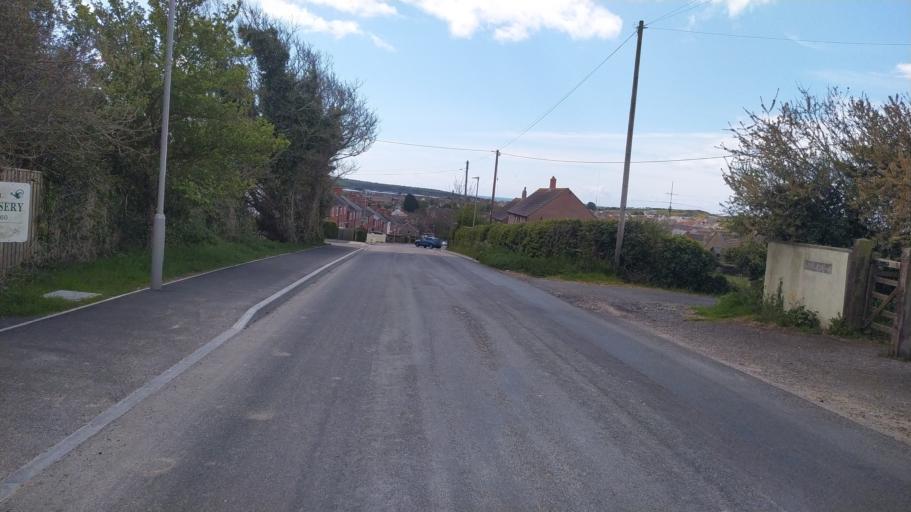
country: GB
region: England
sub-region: Dorset
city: Chickerell
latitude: 50.6269
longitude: -2.4988
